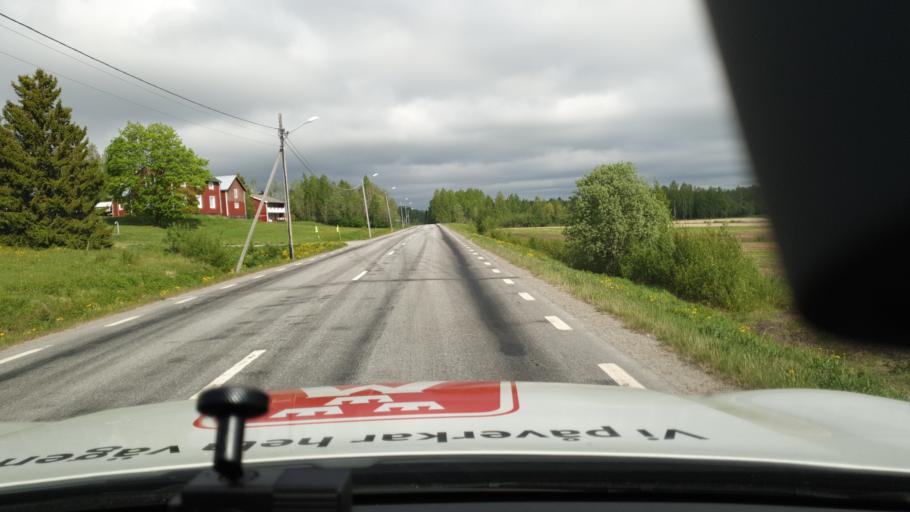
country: SE
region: Vaesterbotten
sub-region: Umea Kommun
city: Roback
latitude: 63.9209
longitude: 20.1906
